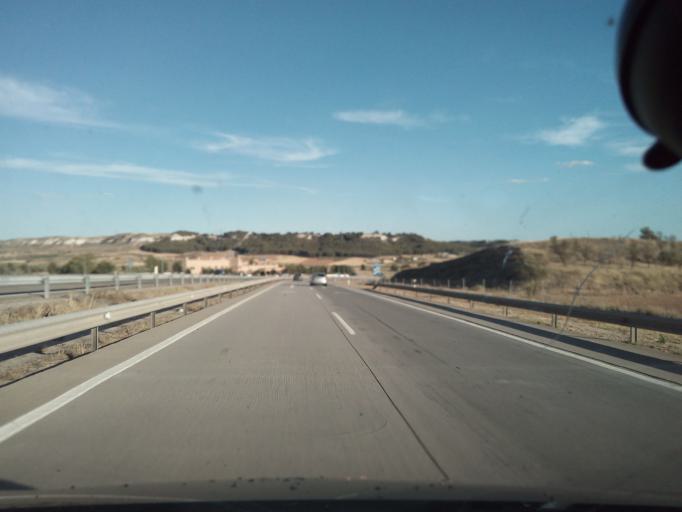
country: ES
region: Castille-La Mancha
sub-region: Province of Toledo
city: Dosbarrios
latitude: 39.8209
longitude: -3.4823
